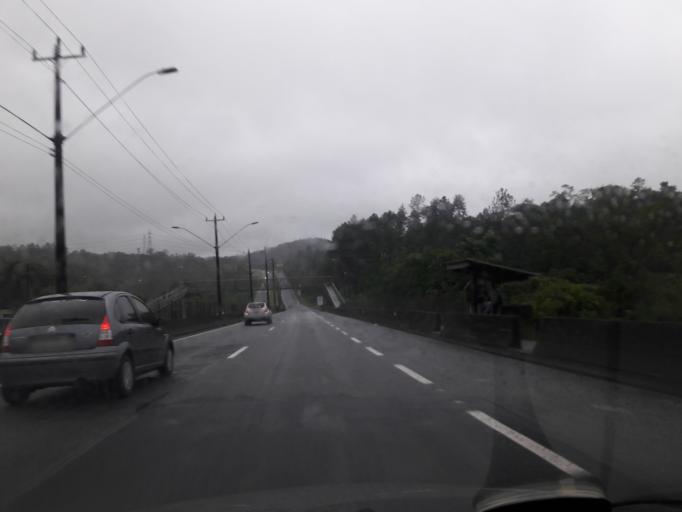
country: BR
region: Sao Paulo
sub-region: Sao Lourenco Da Serra
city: Sao Lourenco da Serra
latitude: -23.8203
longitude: -46.9247
